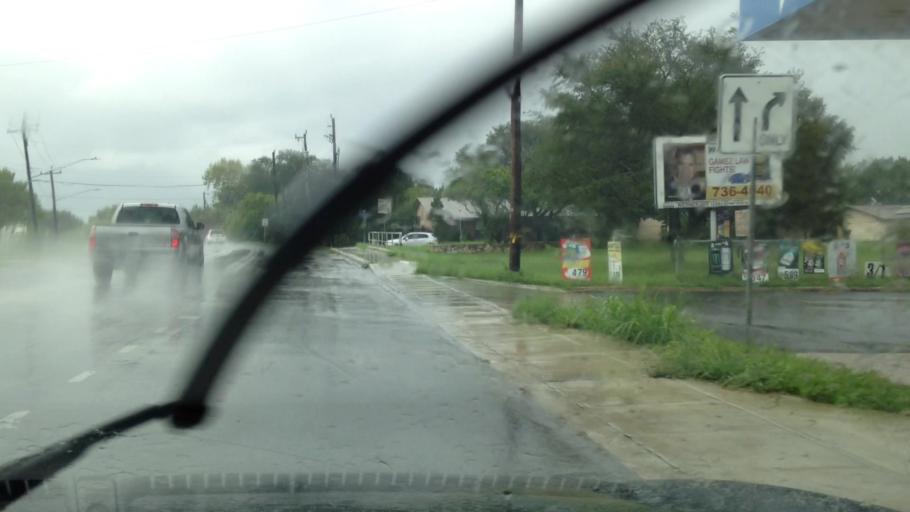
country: US
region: Texas
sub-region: Bexar County
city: Windcrest
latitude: 29.5718
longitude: -98.4185
